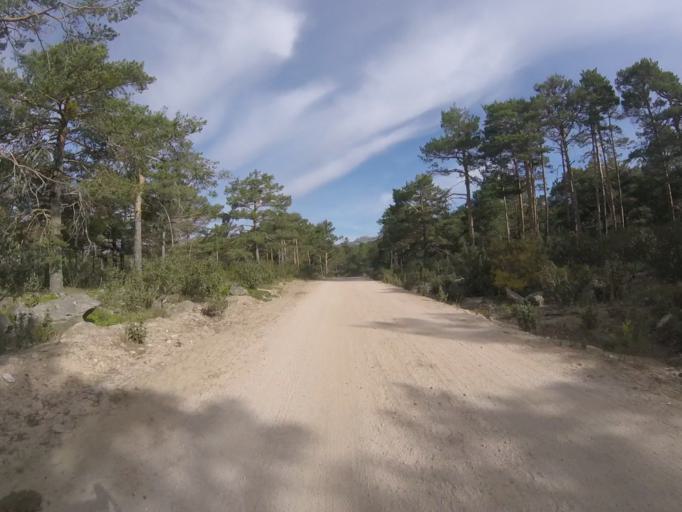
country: ES
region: Castille and Leon
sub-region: Provincia de Avila
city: Peguerinos
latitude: 40.6533
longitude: -4.1818
